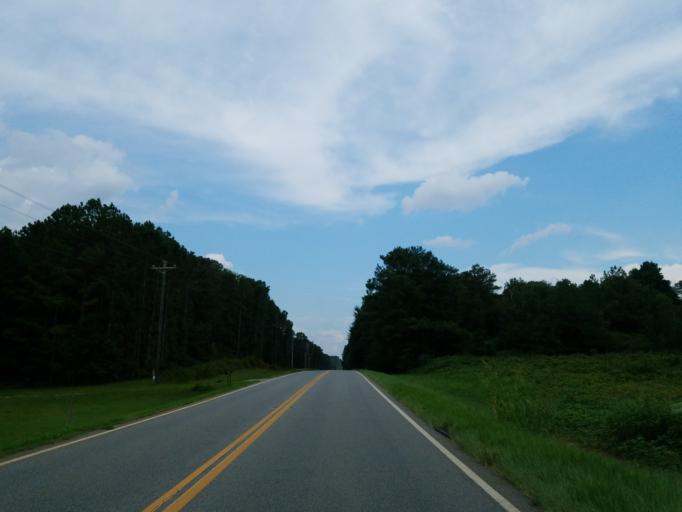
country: US
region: Georgia
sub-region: Dooly County
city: Unadilla
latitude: 32.3291
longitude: -83.7400
